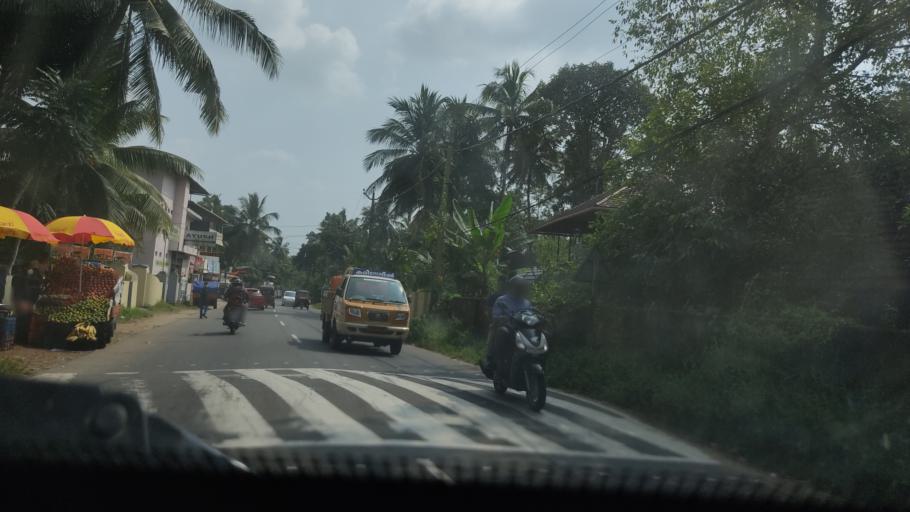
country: IN
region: Kerala
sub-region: Pattanamtitta
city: Tiruvalla
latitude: 9.3372
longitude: 76.5344
